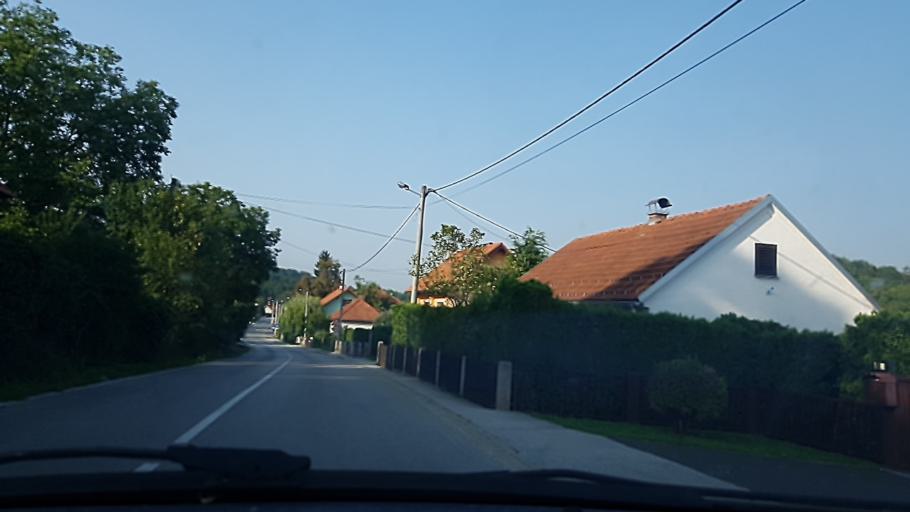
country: HR
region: Zagrebacka
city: Jakovlje
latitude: 45.9577
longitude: 15.8185
